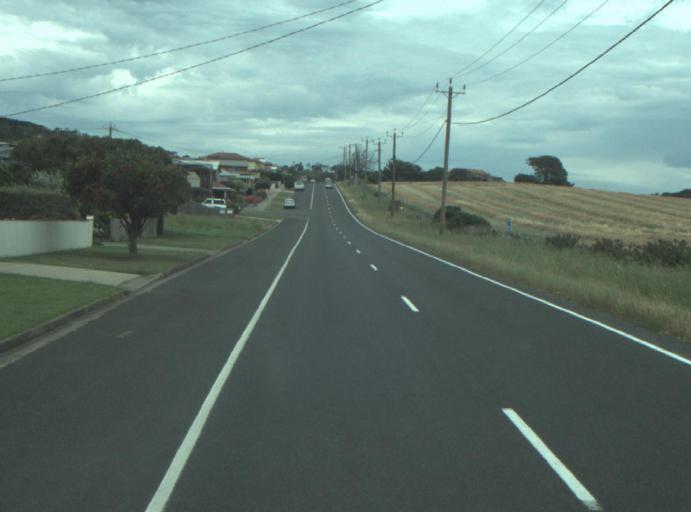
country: AU
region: Victoria
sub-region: Greater Geelong
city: Clifton Springs
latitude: -38.1207
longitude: 144.6278
